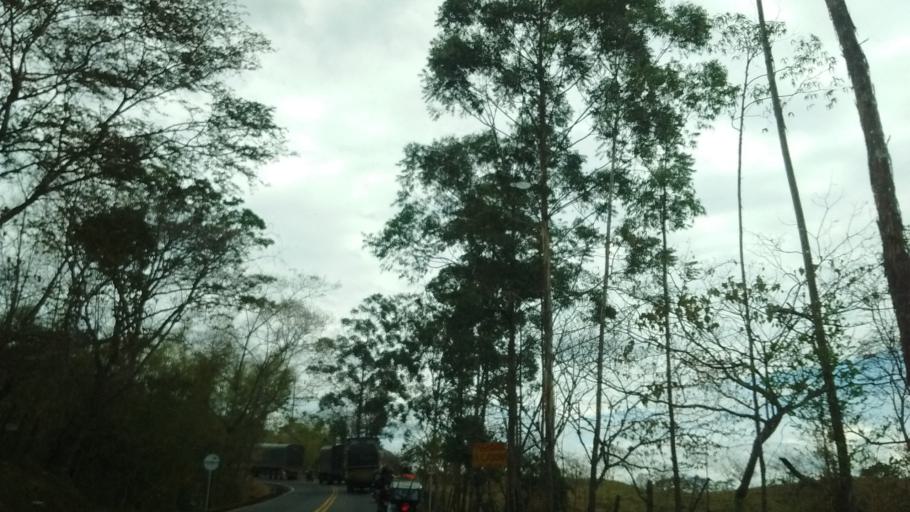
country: CO
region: Cauca
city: Rosas
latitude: 2.2804
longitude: -76.7230
